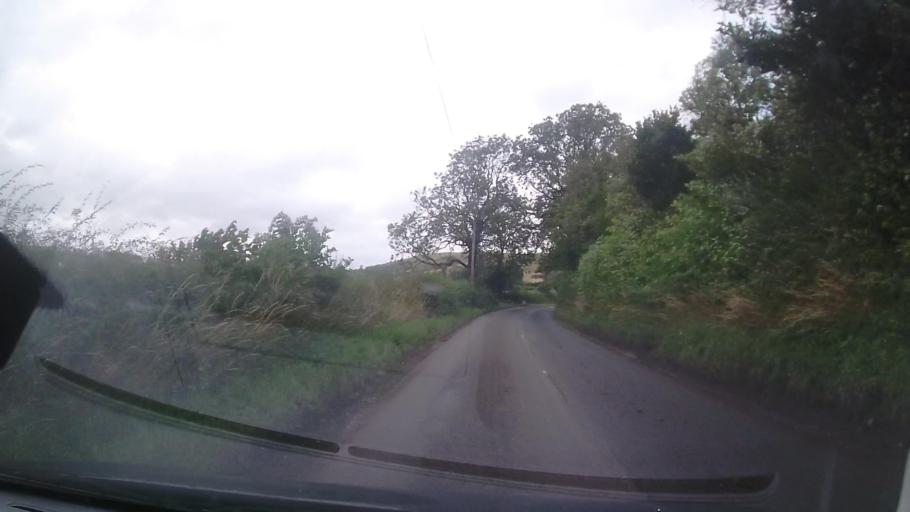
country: GB
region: England
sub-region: Shropshire
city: Pontesbury
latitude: 52.5785
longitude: -2.8847
